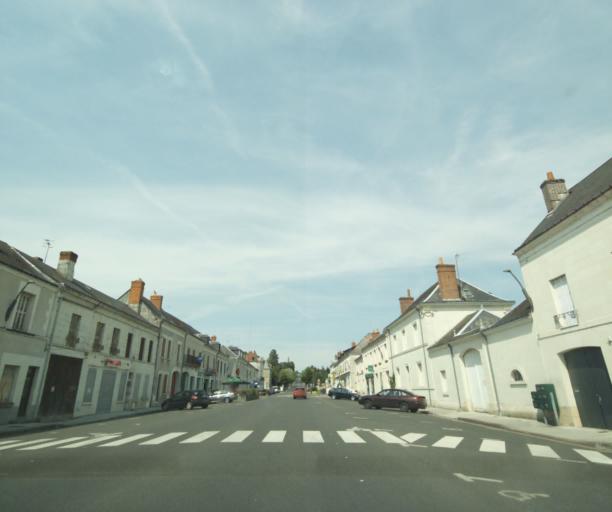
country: FR
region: Centre
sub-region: Departement d'Indre-et-Loire
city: Sainte-Maure-de-Touraine
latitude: 47.1112
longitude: 0.6158
